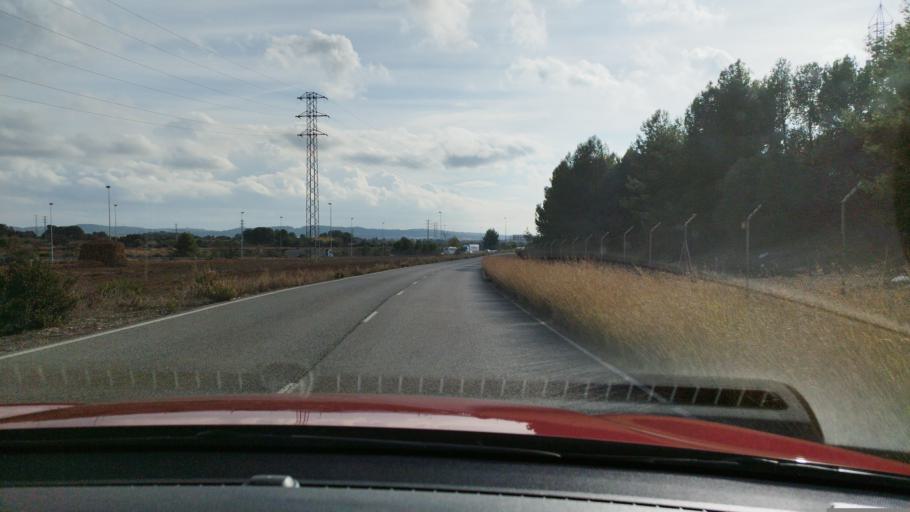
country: ES
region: Catalonia
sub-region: Provincia de Tarragona
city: Santa Oliva
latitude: 41.2648
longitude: 1.5394
